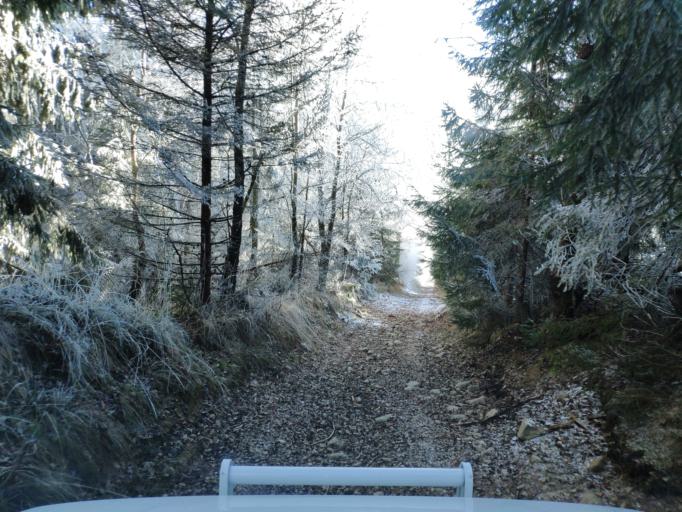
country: SK
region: Kosicky
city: Dobsina
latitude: 48.8148
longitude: 20.4780
